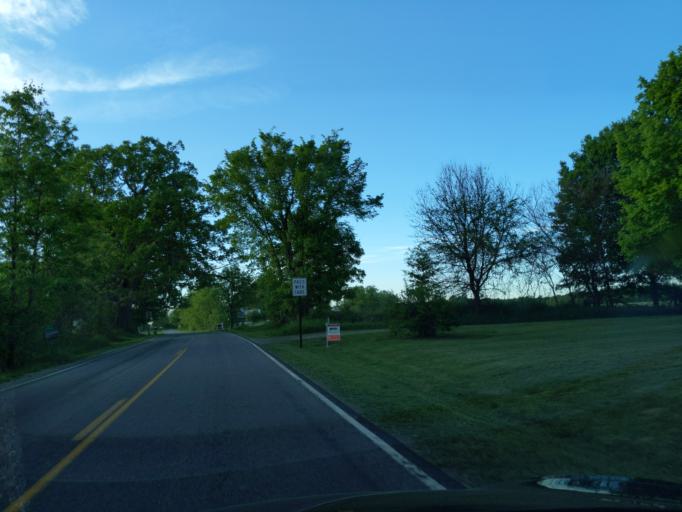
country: US
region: Michigan
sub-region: Ingham County
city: Leslie
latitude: 42.4568
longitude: -84.3136
